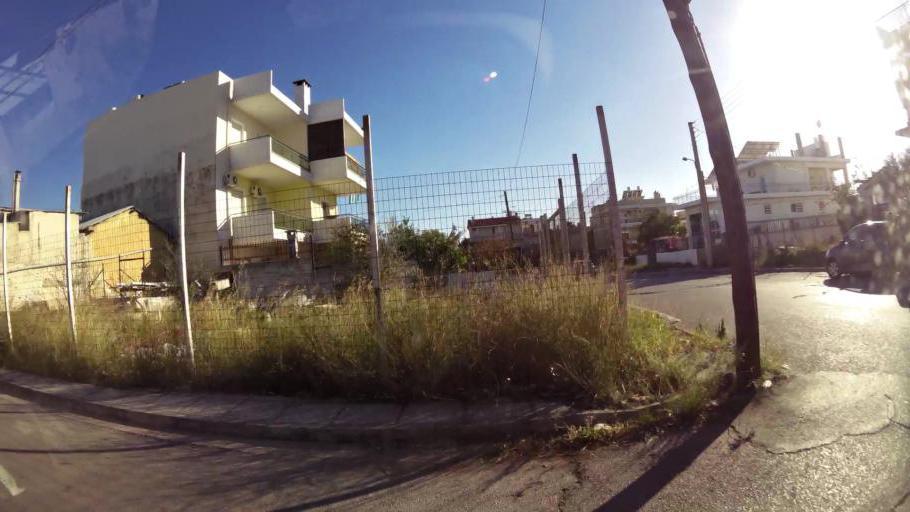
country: GR
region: Attica
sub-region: Nomarchia Anatolikis Attikis
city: Acharnes
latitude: 38.0894
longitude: 23.7293
